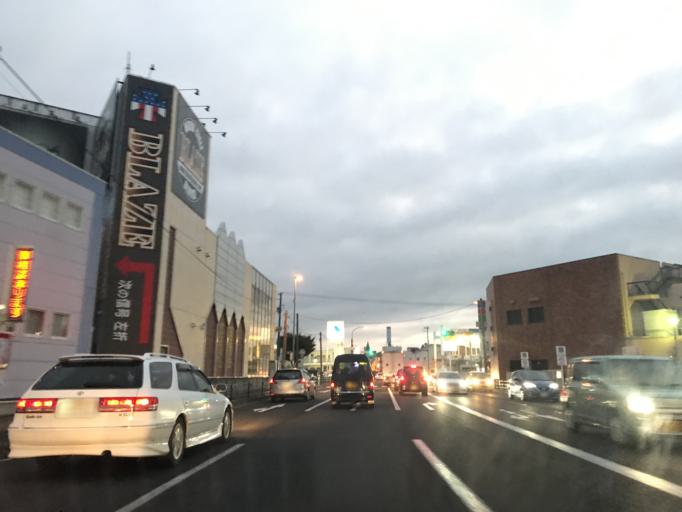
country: JP
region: Fukushima
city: Koriyama
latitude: 37.3867
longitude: 140.3811
